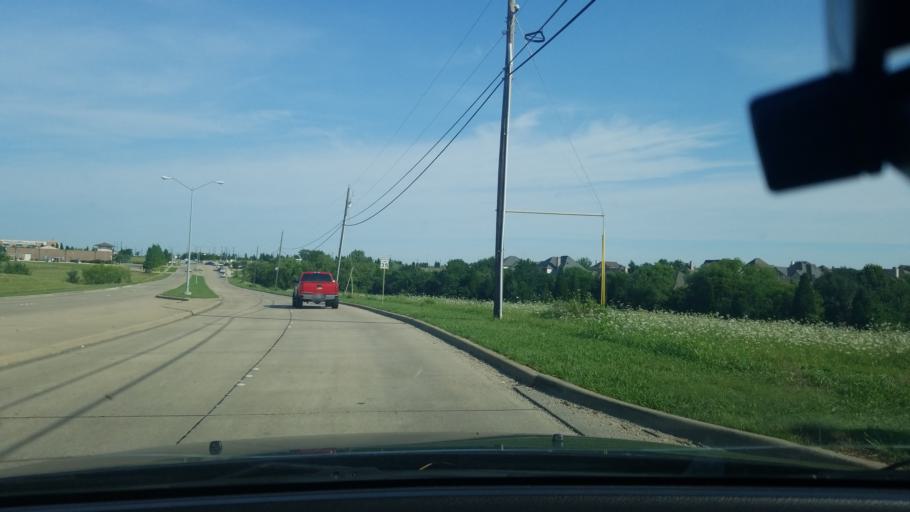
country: US
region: Texas
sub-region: Dallas County
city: Sunnyvale
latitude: 32.7772
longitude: -96.5622
